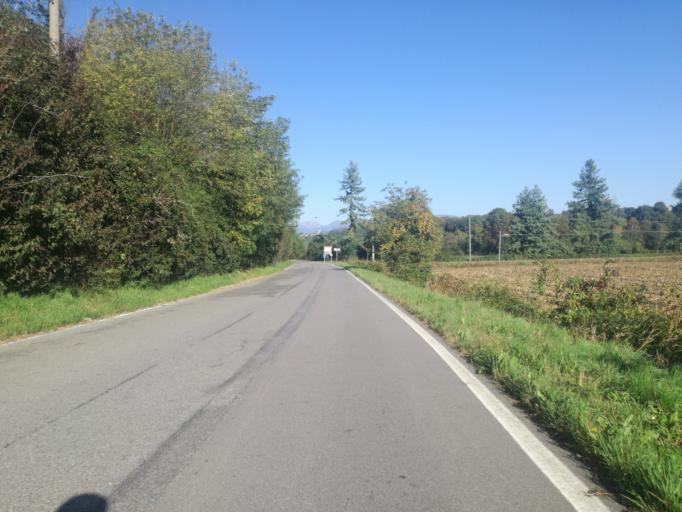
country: IT
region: Lombardy
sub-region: Citta metropolitana di Milano
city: Trezzo sull'Adda
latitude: 45.6193
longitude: 9.5120
